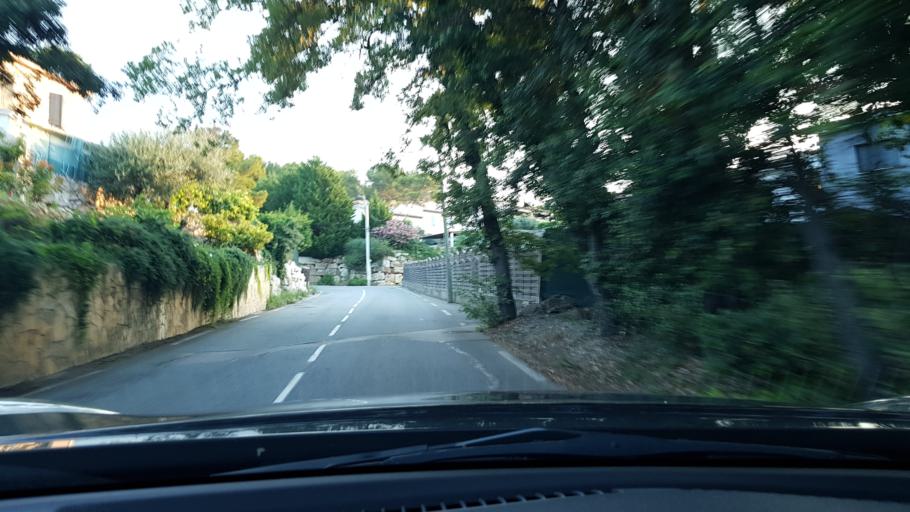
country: FR
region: Provence-Alpes-Cote d'Azur
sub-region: Departement des Alpes-Maritimes
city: Vallauris
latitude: 43.5862
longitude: 7.0462
